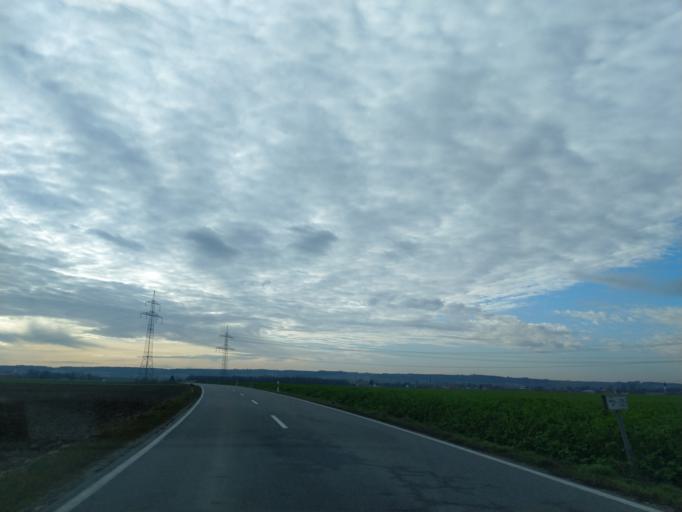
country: DE
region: Bavaria
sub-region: Lower Bavaria
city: Buchhofen
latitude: 48.7068
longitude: 12.9421
